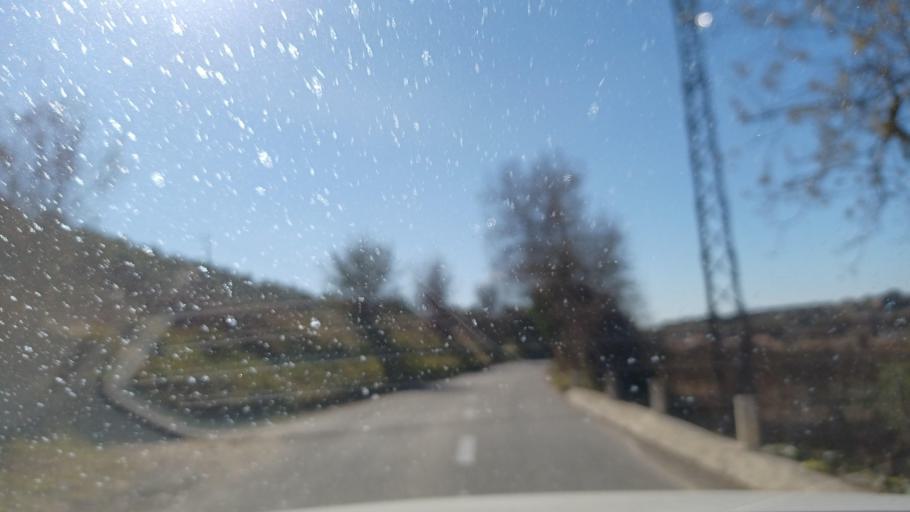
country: ES
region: Catalonia
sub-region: Provincia de Barcelona
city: Vilafranca del Penedes
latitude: 41.3598
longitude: 1.6736
